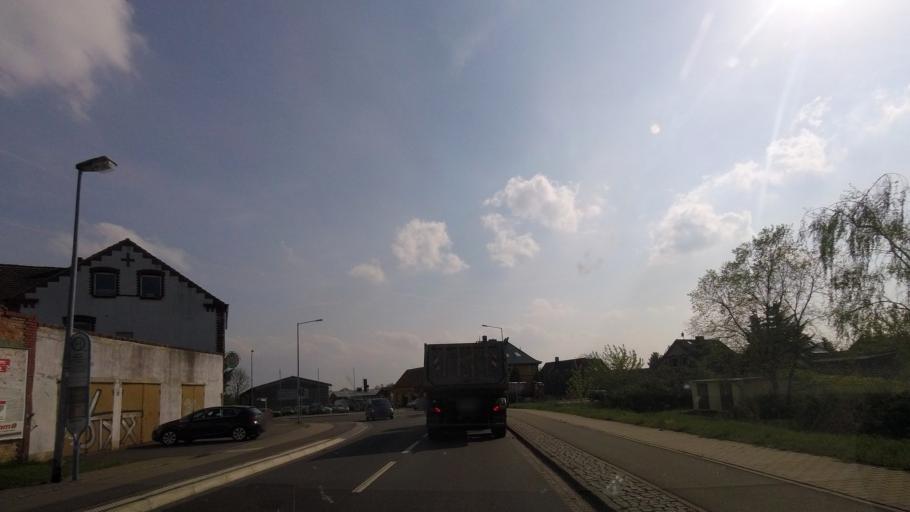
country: DE
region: Saxony-Anhalt
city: Abtsdorf
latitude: 51.8652
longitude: 12.6922
